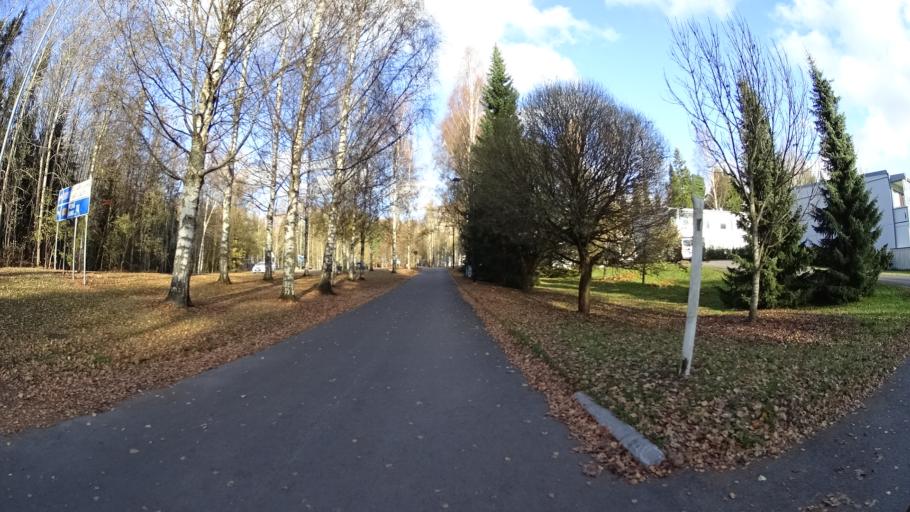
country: FI
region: Uusimaa
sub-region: Helsinki
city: Kilo
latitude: 60.2732
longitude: 24.8393
